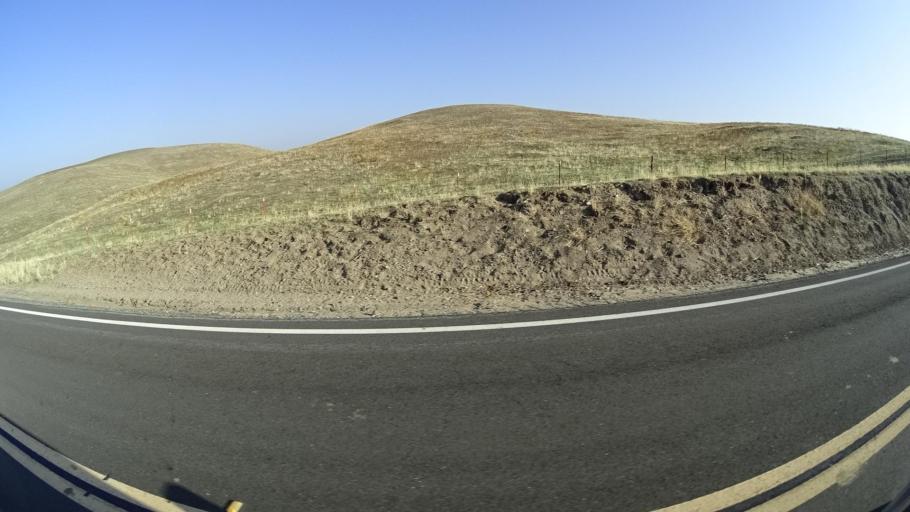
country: US
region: California
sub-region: Tulare County
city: Richgrove
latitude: 35.7462
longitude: -118.9232
